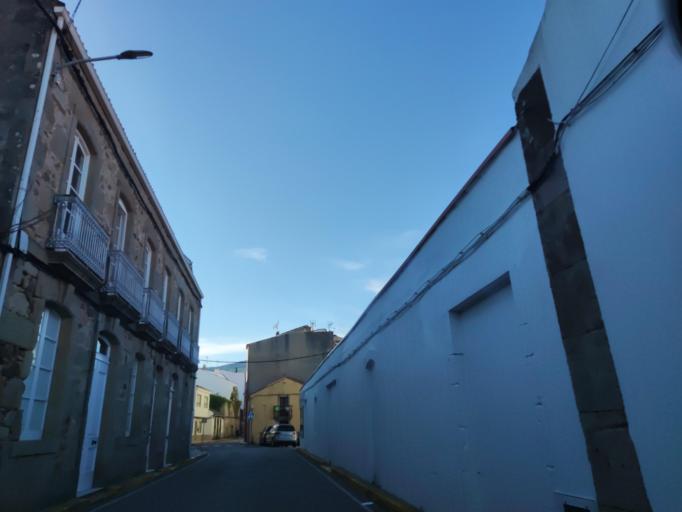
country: ES
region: Galicia
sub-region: Provincia da Coruna
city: Boiro
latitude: 42.6017
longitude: -8.9365
